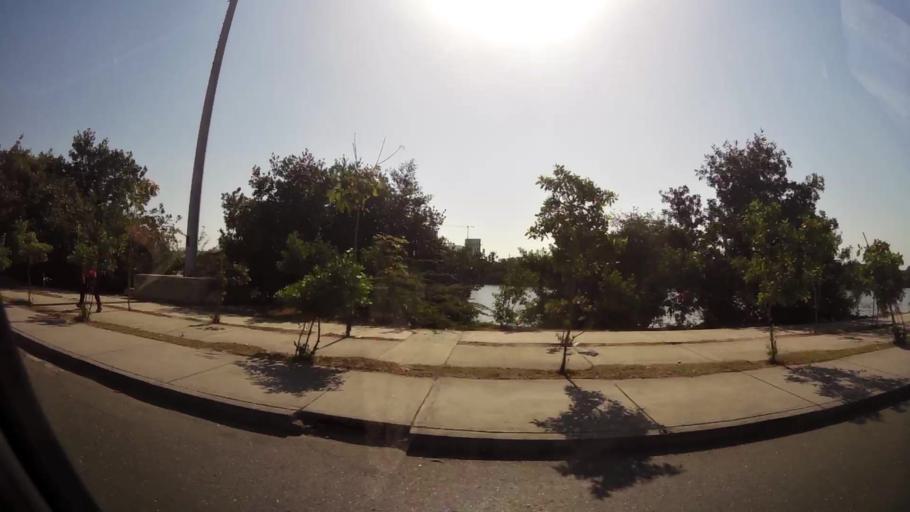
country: CO
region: Bolivar
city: Cartagena
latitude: 10.4296
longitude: -75.5443
